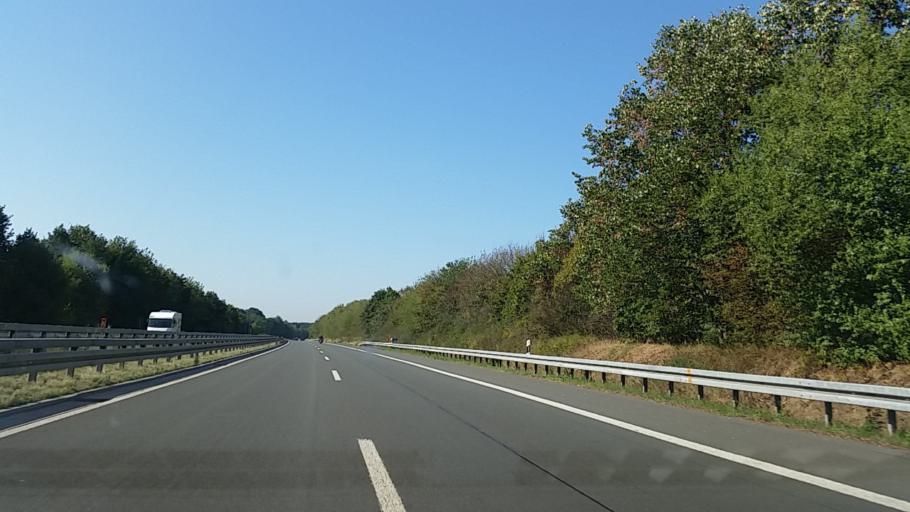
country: DE
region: North Rhine-Westphalia
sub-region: Regierungsbezirk Dusseldorf
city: Langenfeld
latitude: 51.1067
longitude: 6.9713
